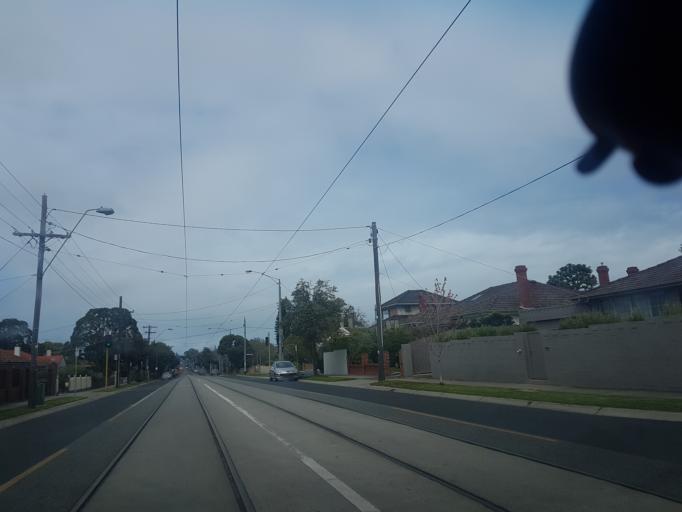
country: AU
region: Victoria
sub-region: Bayside
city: Brighton East
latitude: -37.9044
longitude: 145.0185
